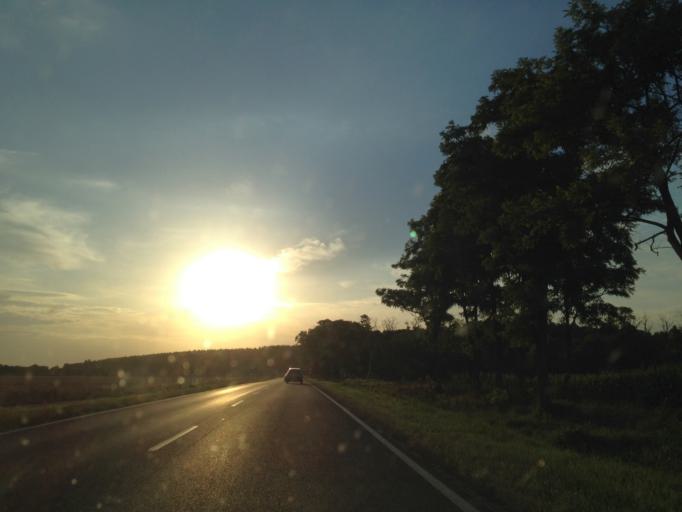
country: HU
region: Gyor-Moson-Sopron
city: Kimle
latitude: 47.8273
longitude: 17.3201
